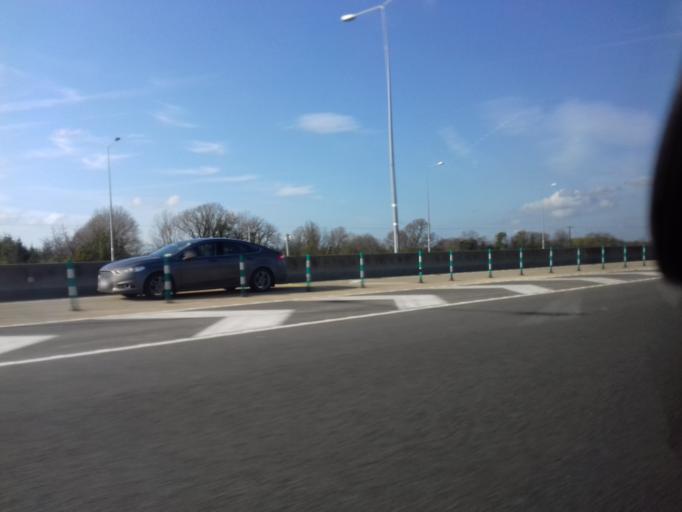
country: IE
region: Leinster
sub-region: Laois
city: Mountrath
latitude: 53.0013
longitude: -7.3912
